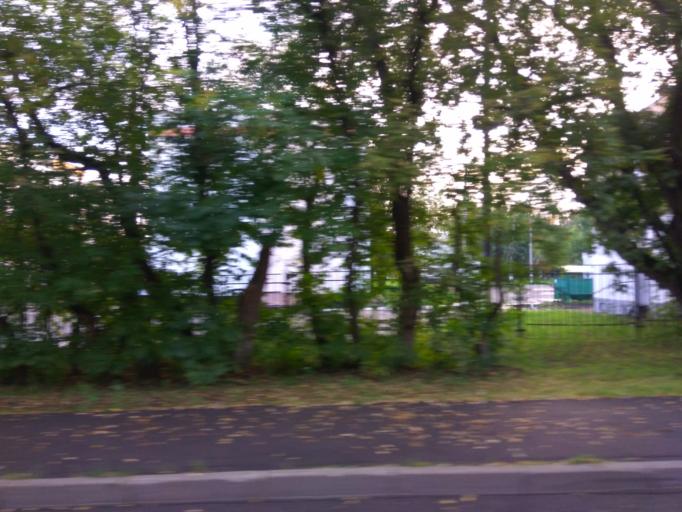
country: RU
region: Moskovskaya
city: Bogorodskoye
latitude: 55.8182
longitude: 37.7164
